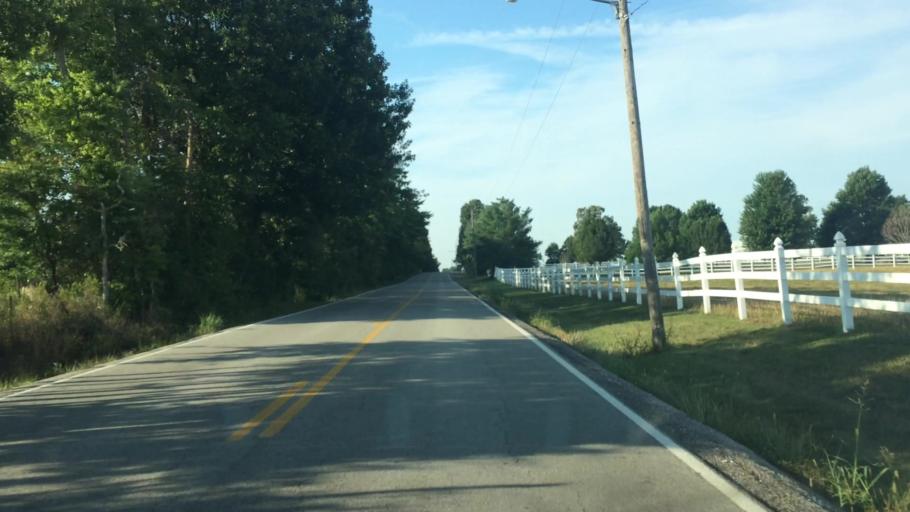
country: US
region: Missouri
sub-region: Greene County
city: Strafford
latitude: 37.2664
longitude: -93.1877
